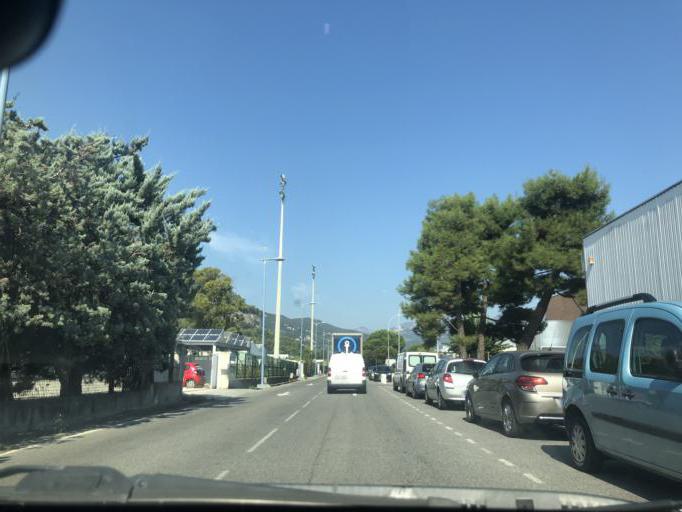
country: FR
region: Provence-Alpes-Cote d'Azur
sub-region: Departement des Alpes-Maritimes
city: Carros
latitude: 43.7926
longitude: 7.2033
